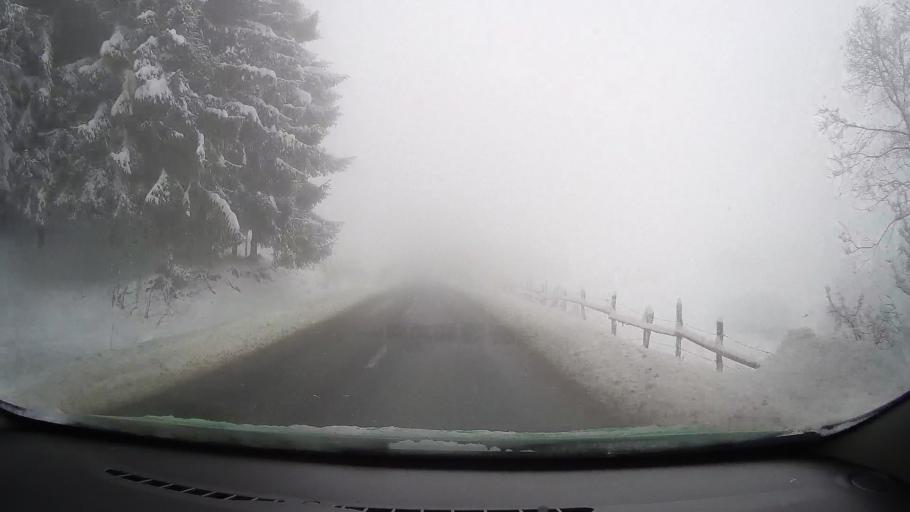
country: RO
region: Sibiu
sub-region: Comuna Jina
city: Jina
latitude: 45.7938
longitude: 23.7018
